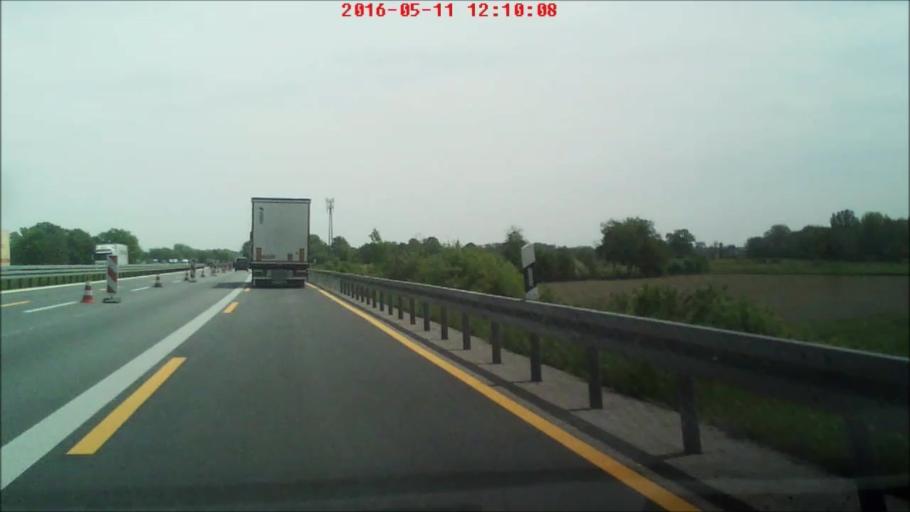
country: DE
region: Bavaria
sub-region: Lower Bavaria
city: Offenberg
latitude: 48.8642
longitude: 12.8478
